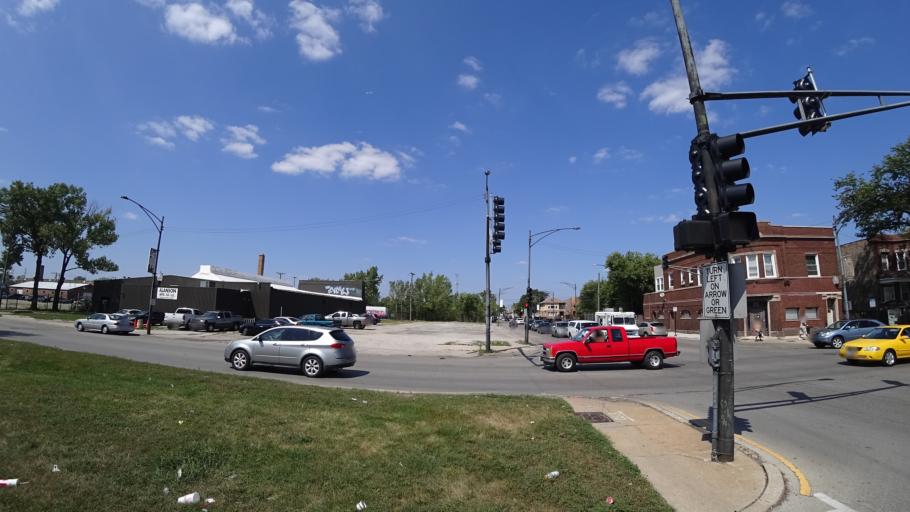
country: US
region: Illinois
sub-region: Cook County
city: Cicero
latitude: 41.8514
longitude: -87.7347
